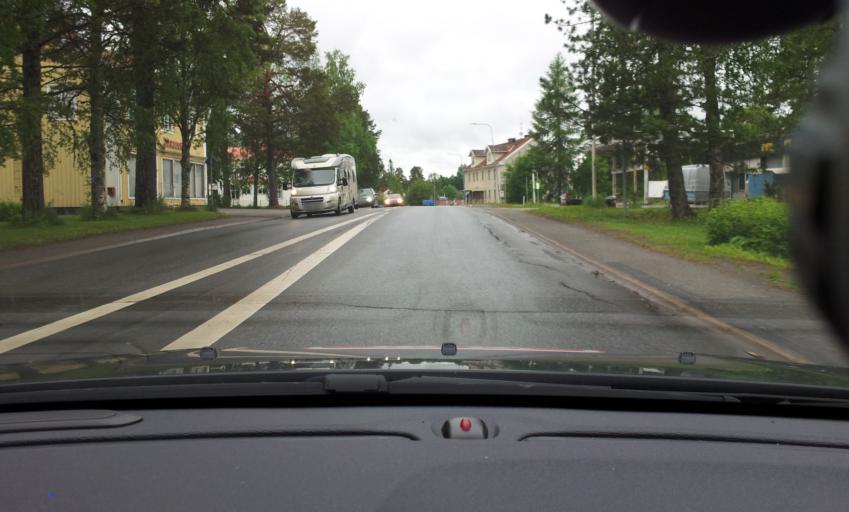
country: SE
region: Jaemtland
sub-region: Stroemsunds Kommun
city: Stroemsund
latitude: 63.5850
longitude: 15.3523
